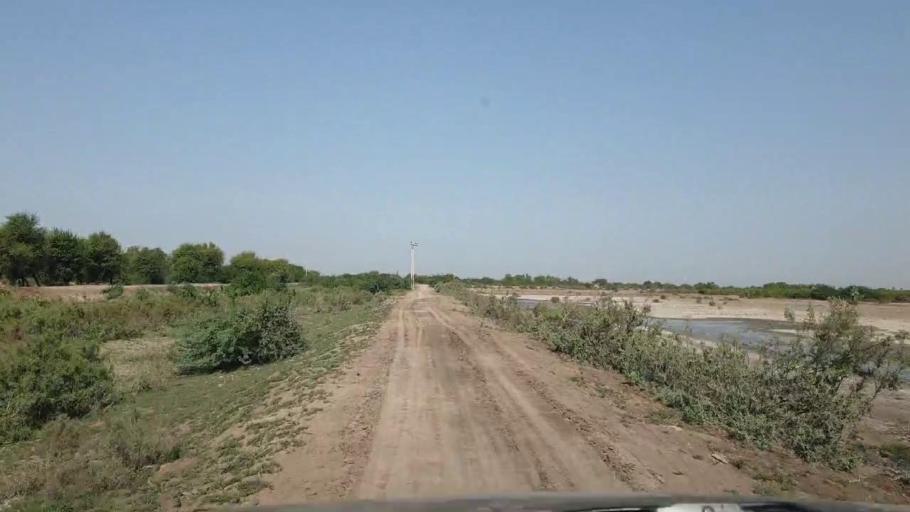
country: PK
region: Sindh
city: Tando Bago
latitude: 24.6619
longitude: 69.0681
